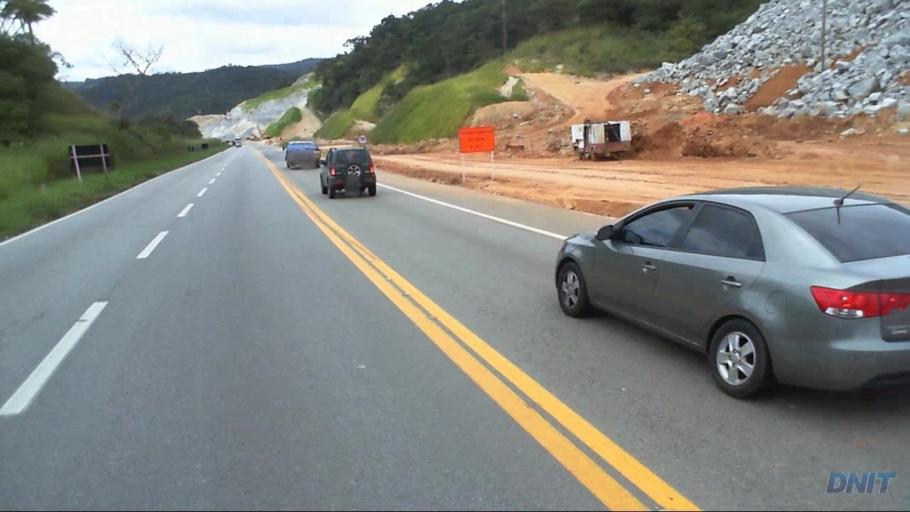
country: BR
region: Minas Gerais
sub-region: Caete
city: Caete
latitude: -19.7878
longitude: -43.6716
